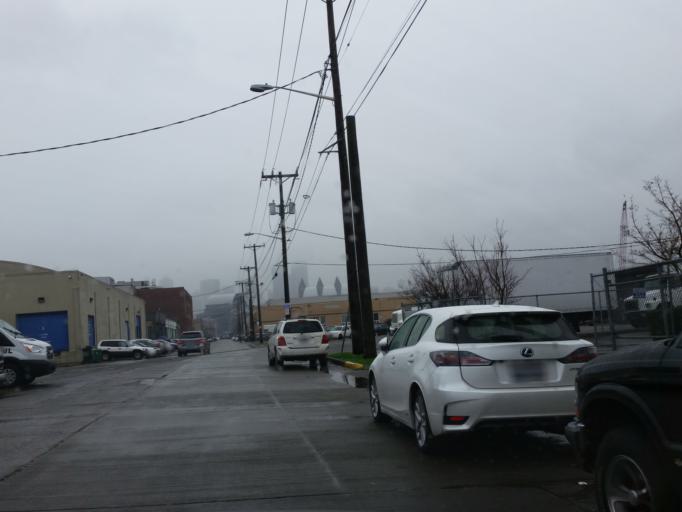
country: US
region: Washington
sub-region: King County
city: Seattle
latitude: 47.5816
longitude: -122.3333
